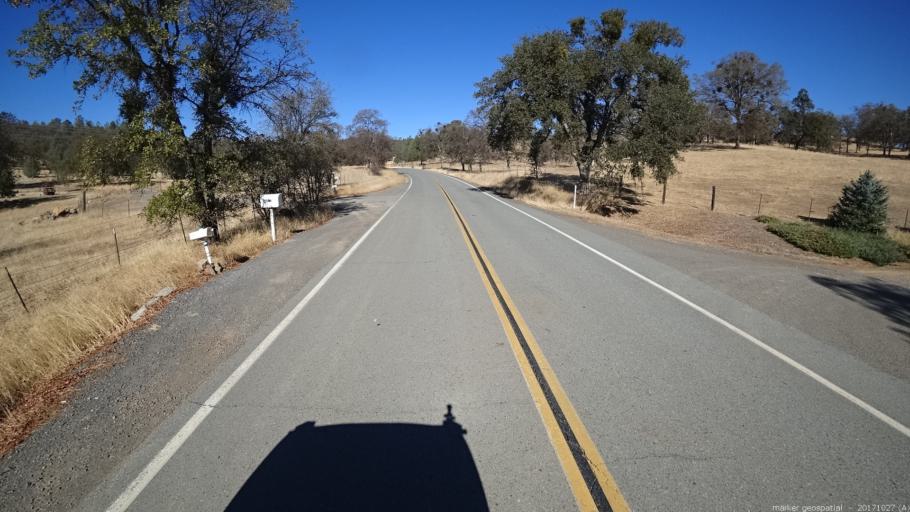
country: US
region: California
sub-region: Shasta County
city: Bella Vista
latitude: 40.7011
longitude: -122.0386
